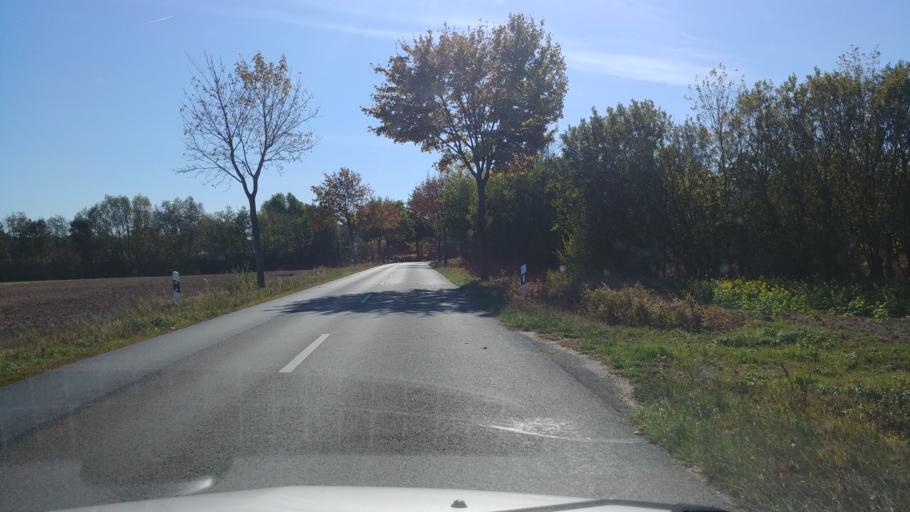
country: DE
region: Lower Saxony
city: Didderse
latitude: 52.3991
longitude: 10.4229
